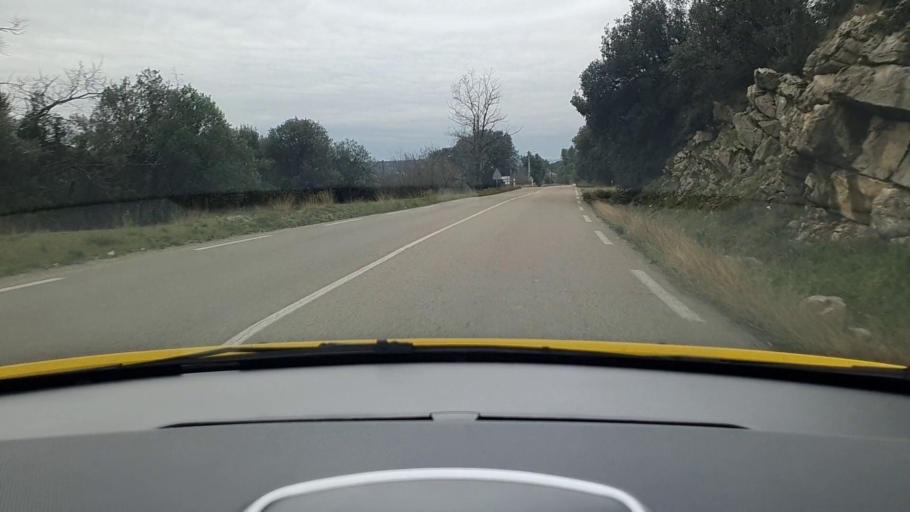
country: FR
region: Languedoc-Roussillon
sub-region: Departement du Gard
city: Saint-Martin-de-Valgalgues
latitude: 44.1719
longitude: 4.0836
